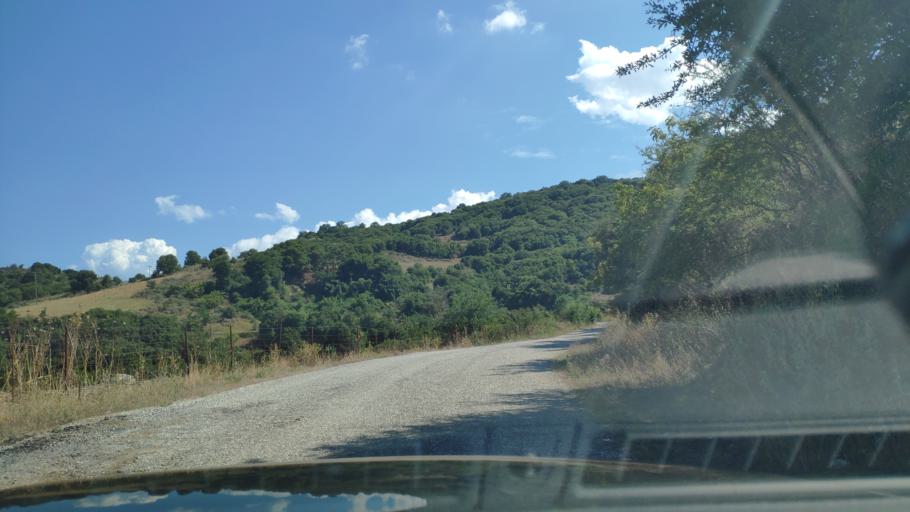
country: GR
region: West Greece
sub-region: Nomos Aitolias kai Akarnanias
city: Katouna
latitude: 38.8094
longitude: 21.1075
